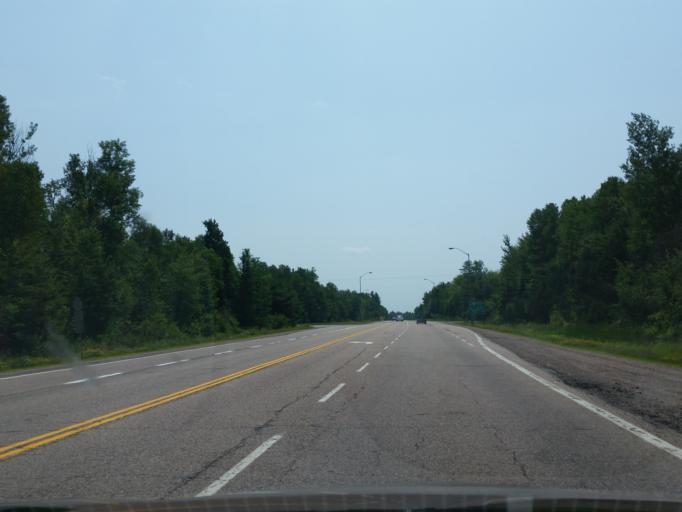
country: CA
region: Ontario
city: Petawawa
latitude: 45.8822
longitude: -77.3044
